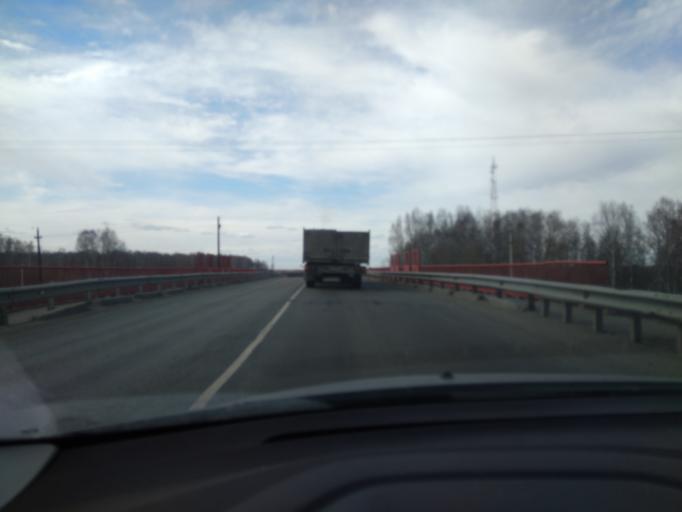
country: RU
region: Sverdlovsk
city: Pyshma
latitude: 56.9565
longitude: 63.2345
